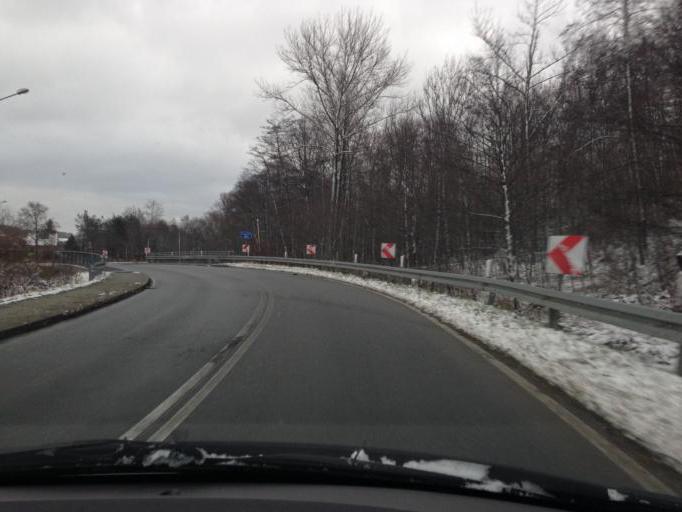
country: PL
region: Lesser Poland Voivodeship
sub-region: Powiat brzeski
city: Gnojnik
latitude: 49.8511
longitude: 20.6262
